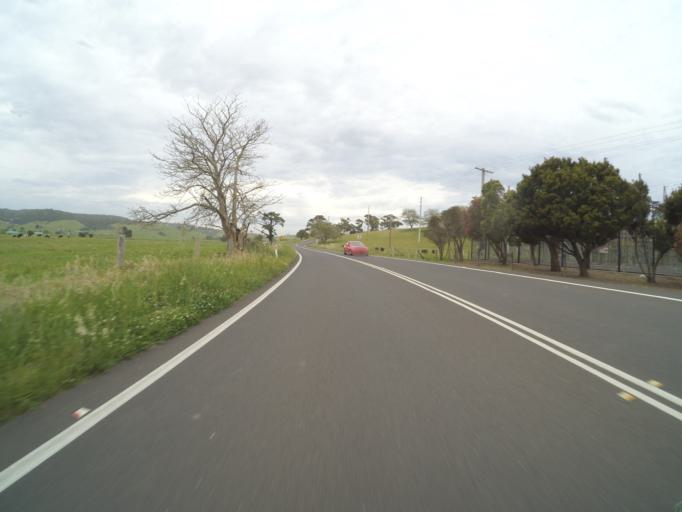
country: AU
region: New South Wales
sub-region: Kiama
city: Jamberoo
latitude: -34.6543
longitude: 150.8110
